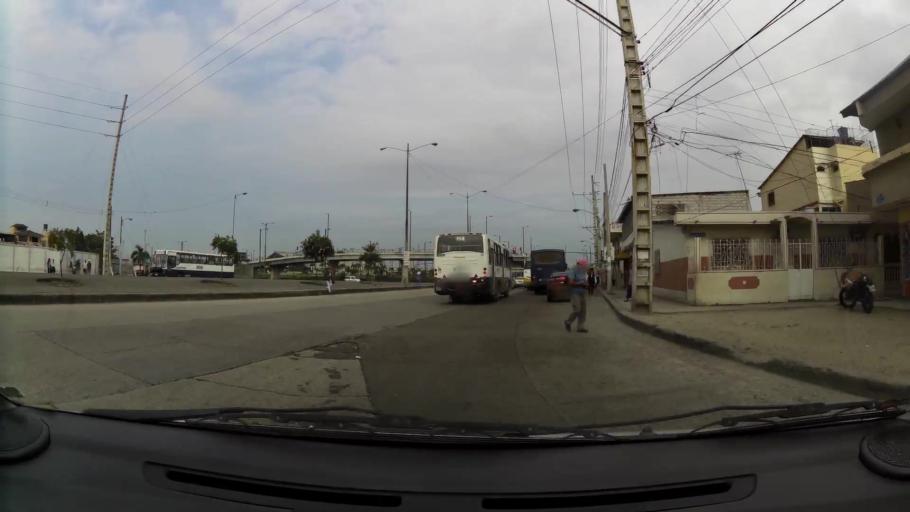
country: EC
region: Guayas
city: Eloy Alfaro
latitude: -2.1384
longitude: -79.8843
